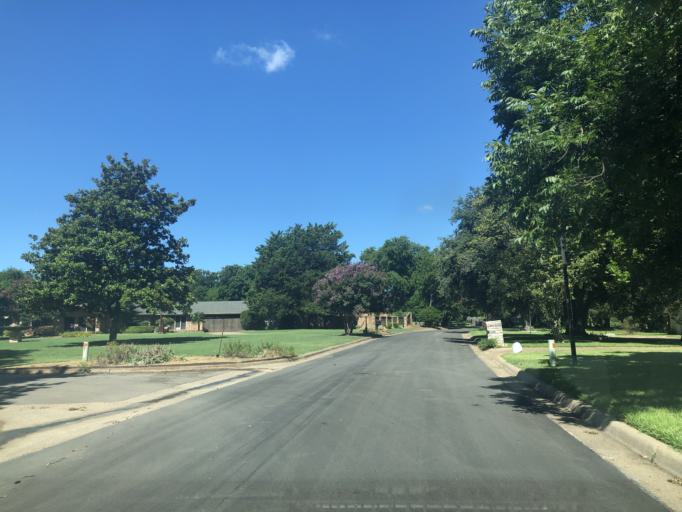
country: US
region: Texas
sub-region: Dallas County
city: Duncanville
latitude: 32.6360
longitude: -96.9355
